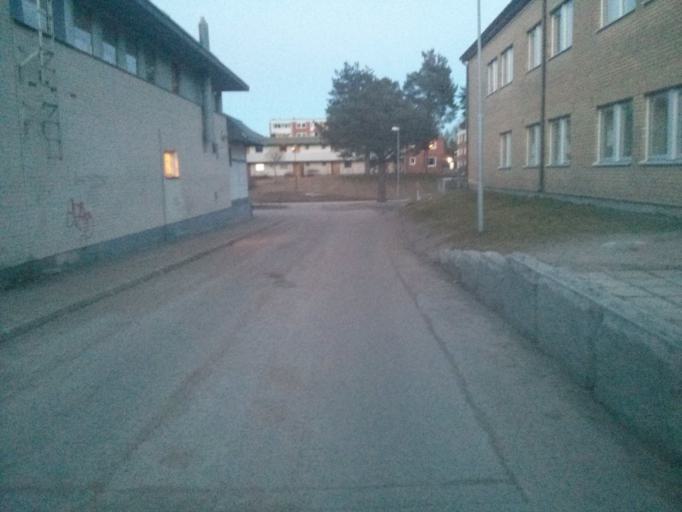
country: SE
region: Vaesternorrland
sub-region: Sundsvalls Kommun
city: Kvissleby
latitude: 62.2979
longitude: 17.3790
